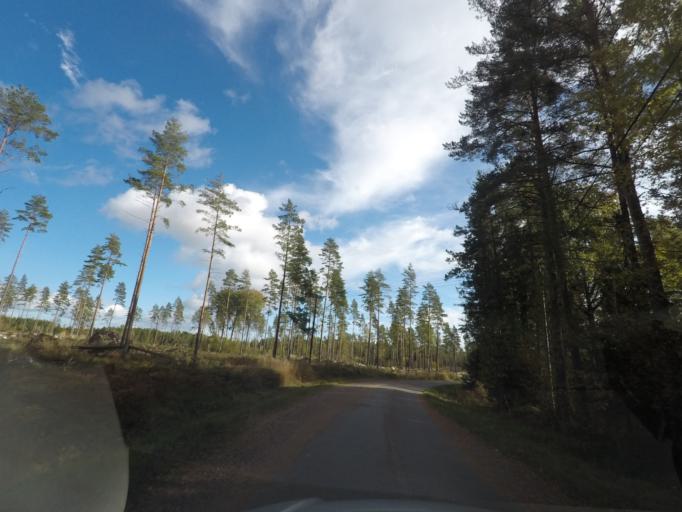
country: SE
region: Vaestmanland
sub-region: Kungsors Kommun
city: Kungsoer
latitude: 59.3382
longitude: 16.2076
